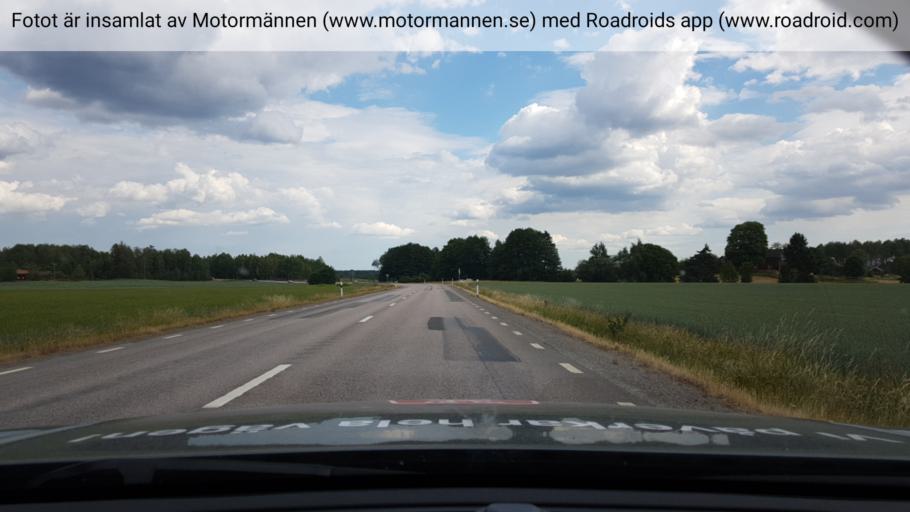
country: SE
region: Uppsala
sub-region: Heby Kommun
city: Morgongava
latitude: 59.9199
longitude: 16.9946
